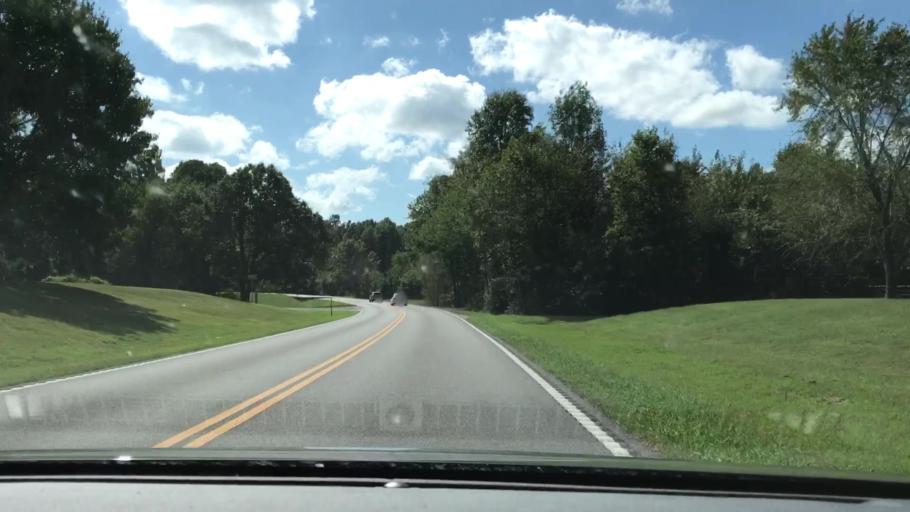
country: US
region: Kentucky
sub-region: McCracken County
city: Reidland
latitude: 36.9701
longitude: -88.5155
